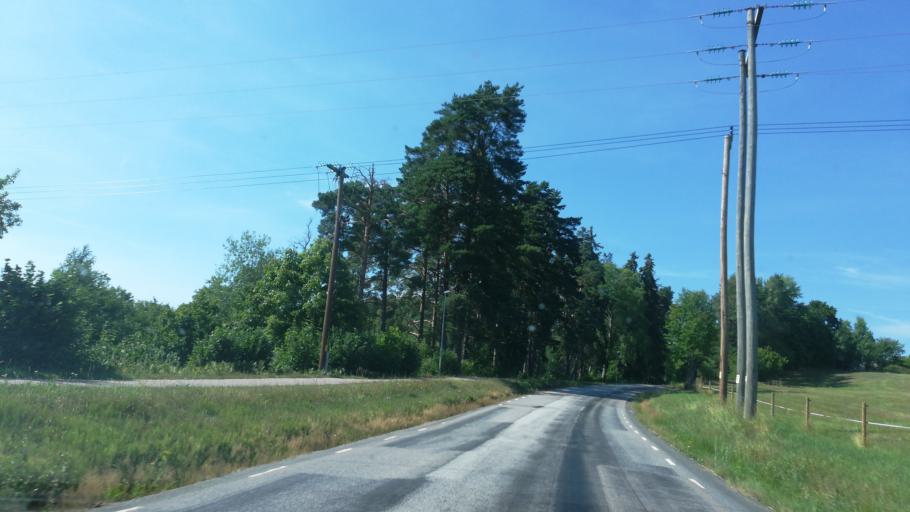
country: SE
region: OEstergoetland
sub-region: Finspangs Kommun
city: Finspang
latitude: 58.7299
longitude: 15.8290
